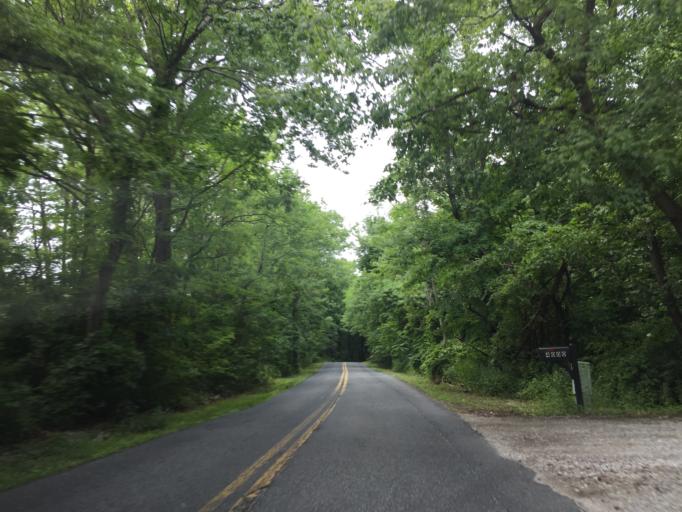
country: US
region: Maryland
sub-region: Baltimore County
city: Edgemere
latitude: 39.2677
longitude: -76.4579
